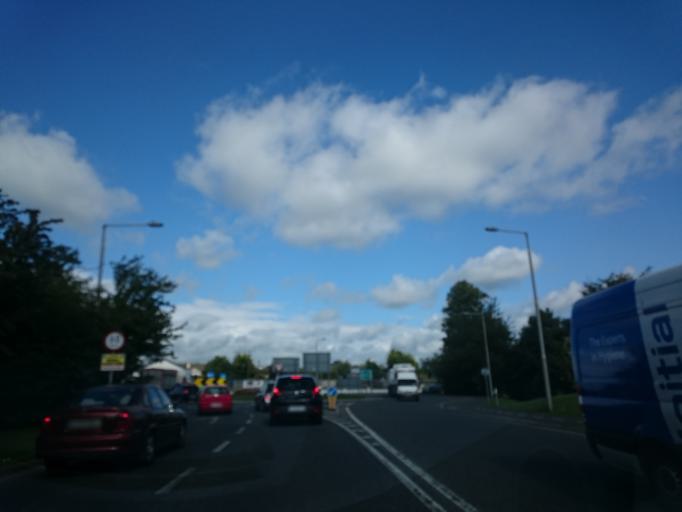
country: IE
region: Leinster
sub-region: Kilkenny
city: Kilkenny
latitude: 52.6423
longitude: -7.2624
